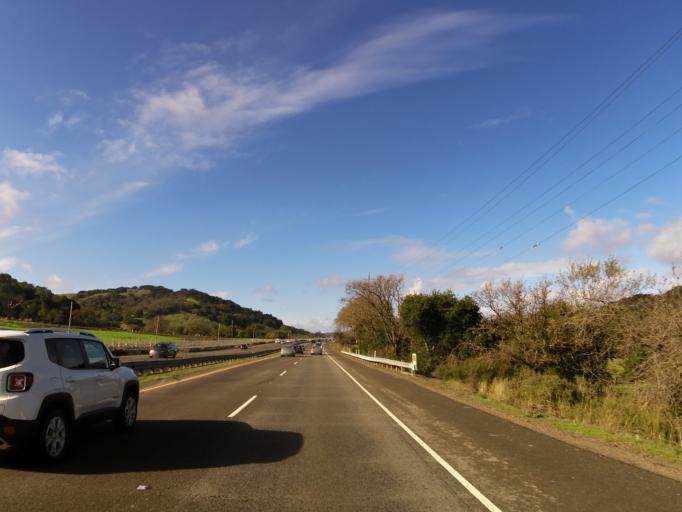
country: US
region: California
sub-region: Marin County
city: Novato
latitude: 38.1690
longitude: -122.5834
